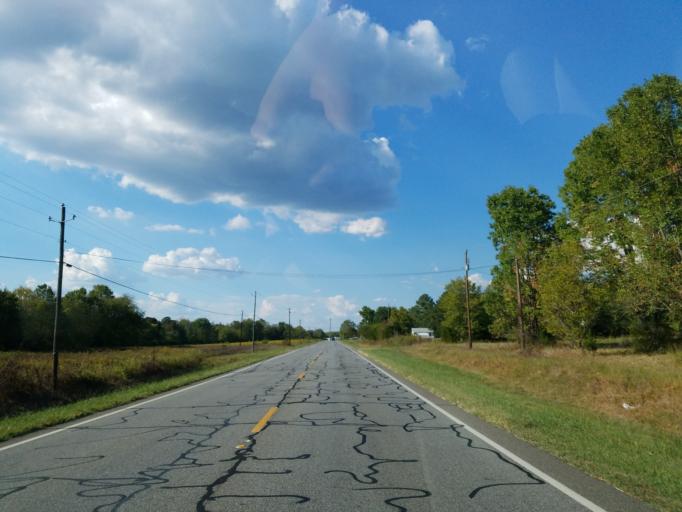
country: US
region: Georgia
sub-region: Bartow County
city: Rydal
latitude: 34.4907
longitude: -84.7073
